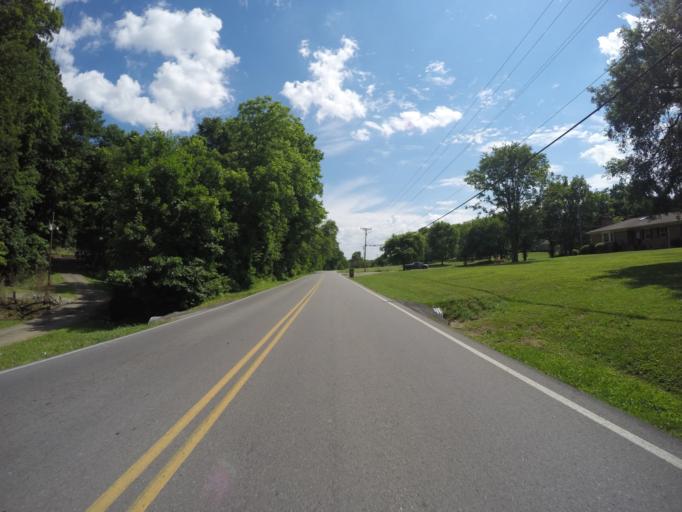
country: US
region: Tennessee
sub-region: Wilson County
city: Green Hill
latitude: 36.2152
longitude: -86.5505
